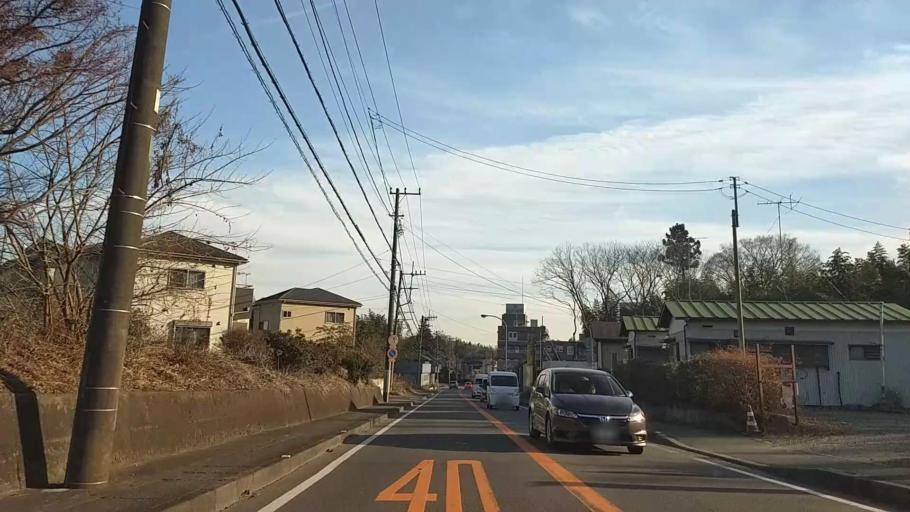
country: JP
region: Kanagawa
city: Zama
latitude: 35.5078
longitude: 139.3073
